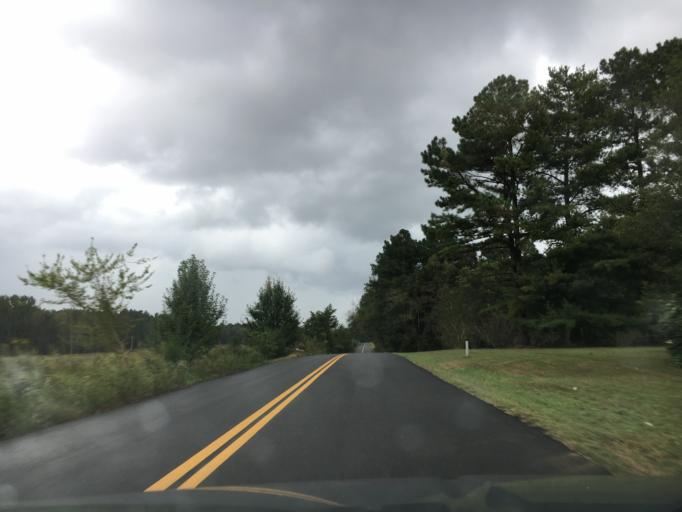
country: US
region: Virginia
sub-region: Amelia County
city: Amelia Court House
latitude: 37.4273
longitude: -77.9579
